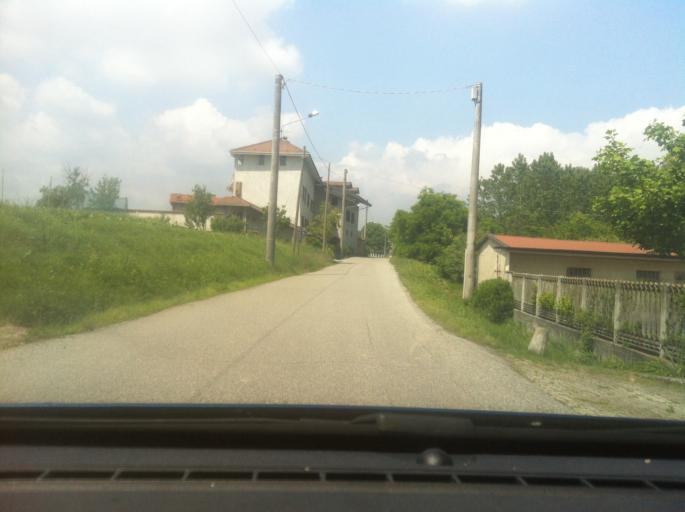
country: IT
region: Piedmont
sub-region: Provincia di Torino
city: Romano Canavese
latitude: 45.4020
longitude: 7.8822
